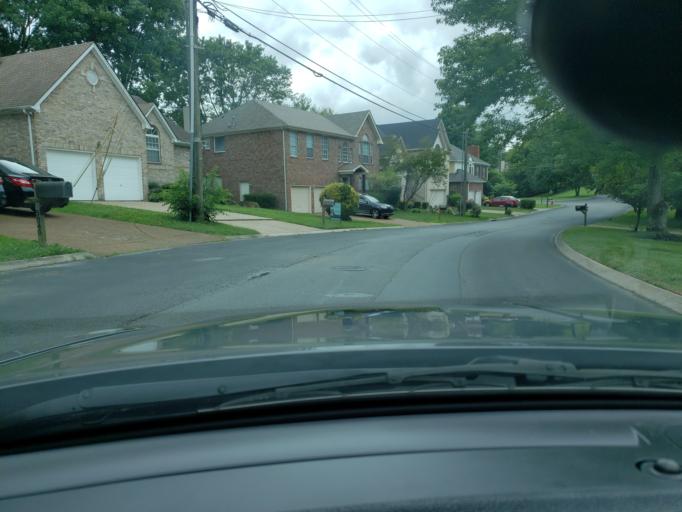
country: US
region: Tennessee
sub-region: Williamson County
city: Nolensville
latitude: 36.0350
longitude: -86.6785
